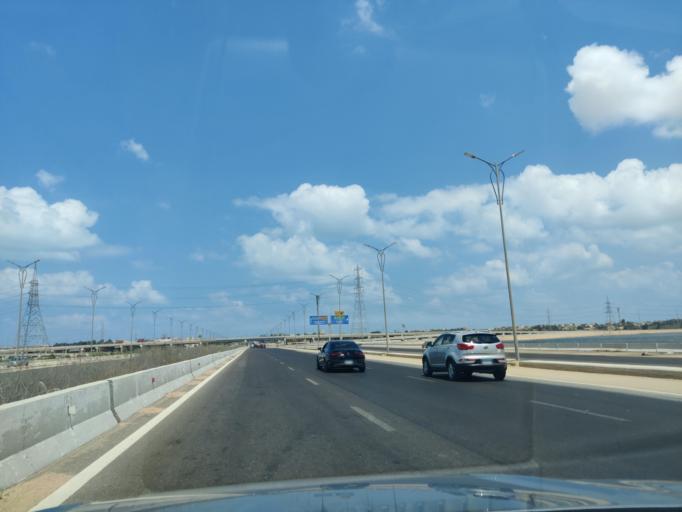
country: EG
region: Alexandria
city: Alexandria
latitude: 30.9990
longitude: 29.6444
